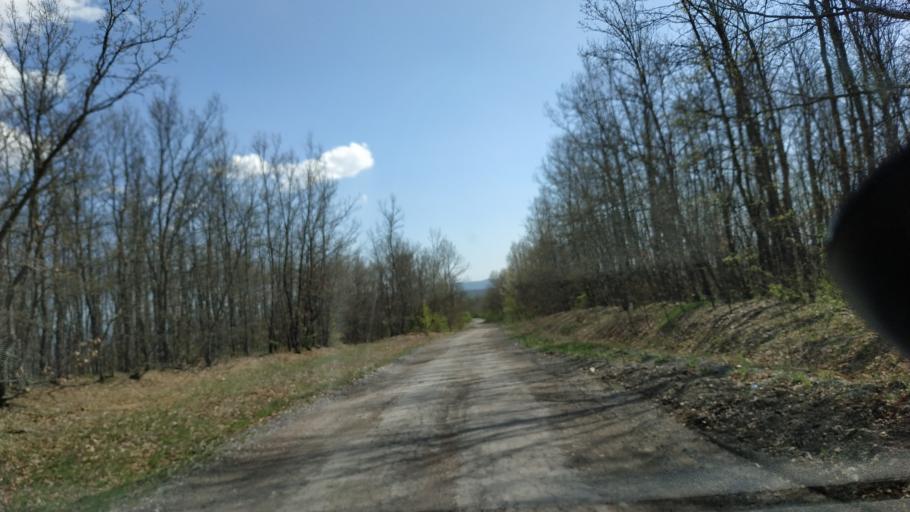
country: RS
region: Central Serbia
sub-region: Zajecarski Okrug
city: Soko Banja
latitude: 43.5360
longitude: 21.9062
